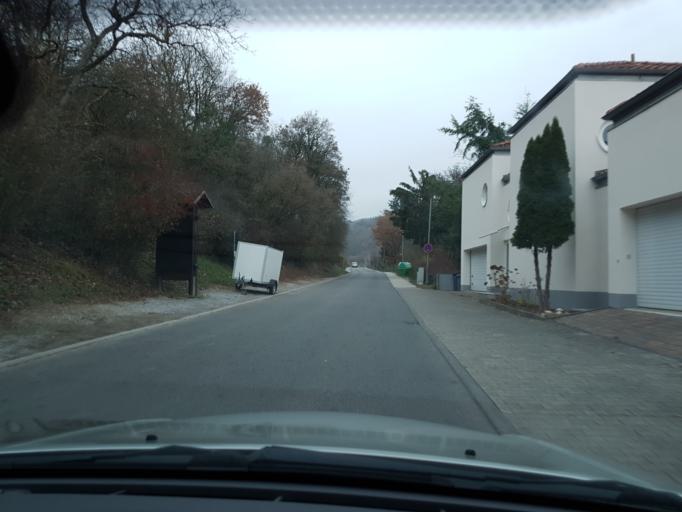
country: DE
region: Hesse
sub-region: Regierungsbezirk Darmstadt
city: Kiedrich
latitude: 50.0469
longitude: 8.0783
